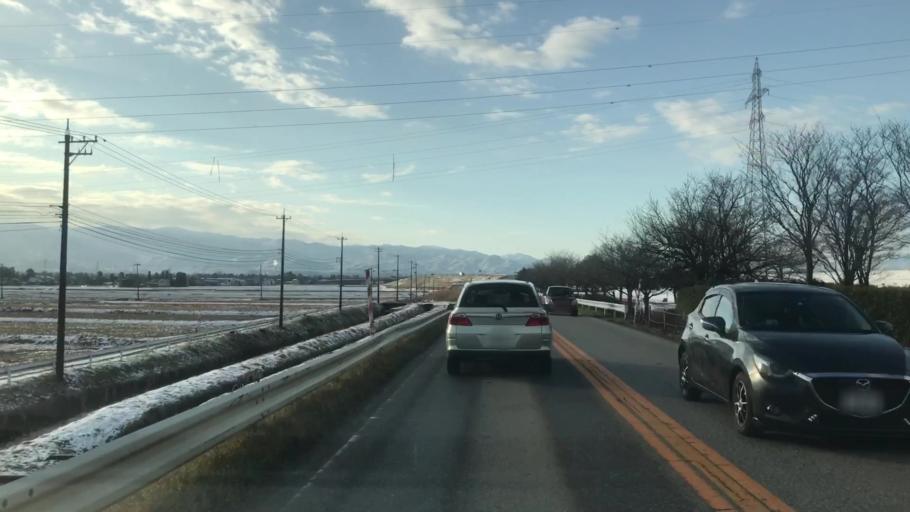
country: JP
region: Toyama
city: Toyama-shi
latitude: 36.6839
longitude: 137.2845
